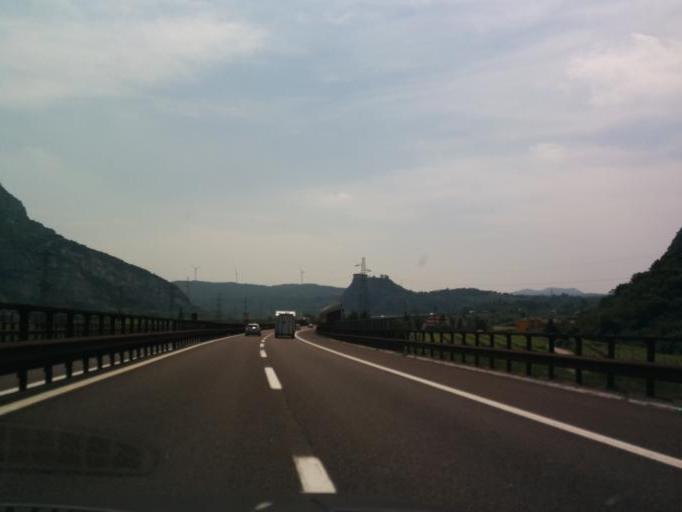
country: IT
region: Veneto
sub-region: Provincia di Verona
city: Dolce
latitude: 45.5885
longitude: 10.8351
